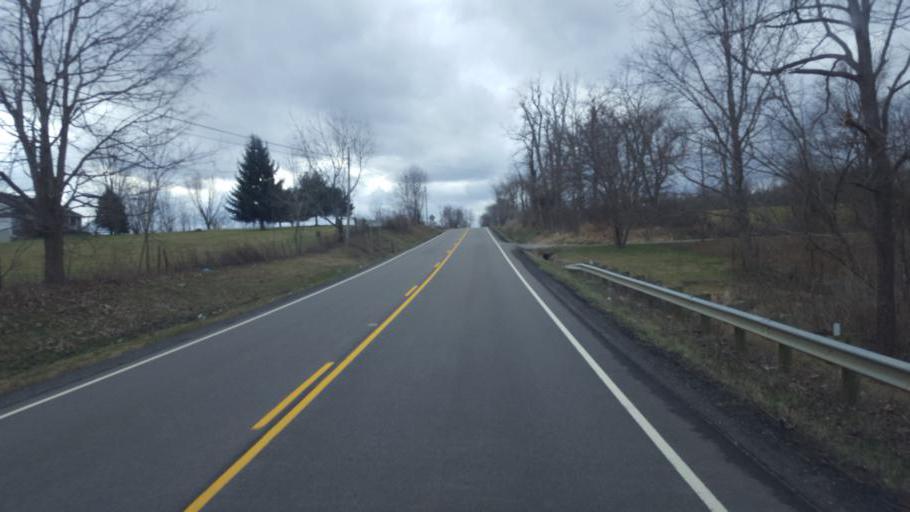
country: US
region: Ohio
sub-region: Knox County
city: Mount Vernon
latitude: 40.3085
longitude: -82.5106
